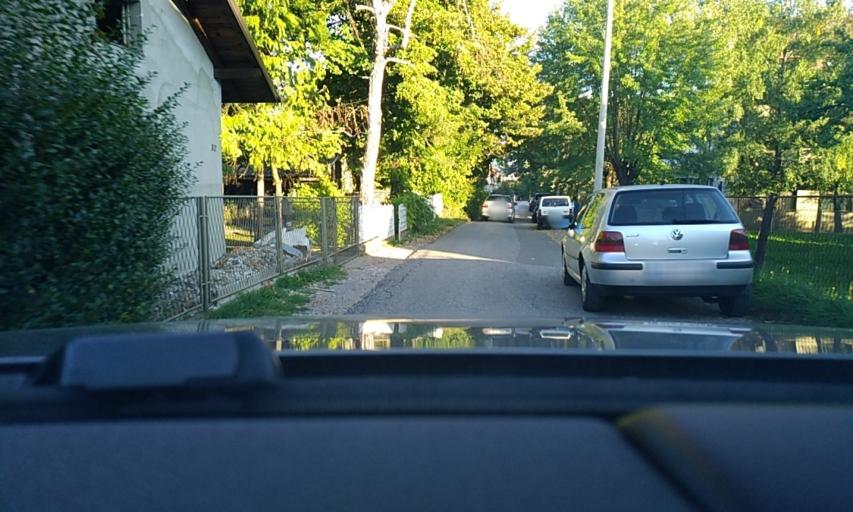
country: BA
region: Republika Srpska
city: Banja Luka
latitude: 44.7830
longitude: 17.1866
